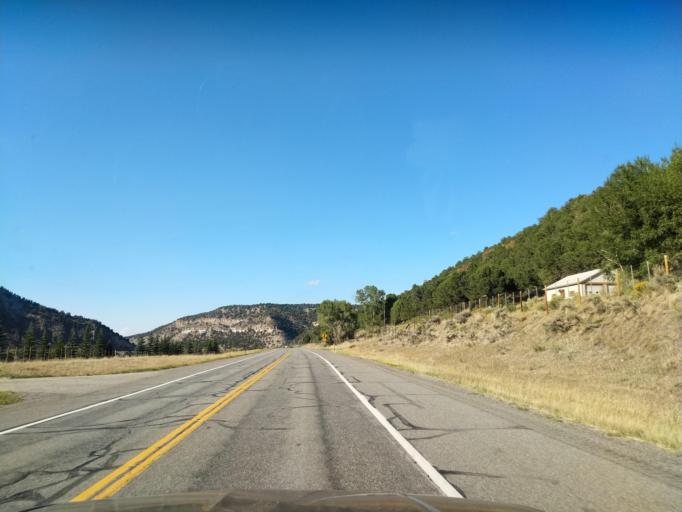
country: US
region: Colorado
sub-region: Ouray County
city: Ouray
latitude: 38.2500
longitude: -107.7587
